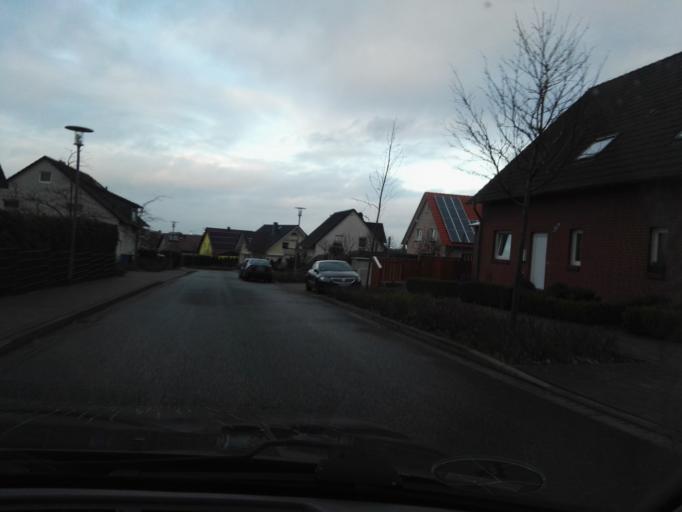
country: DE
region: Lower Saxony
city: Leiferde
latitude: 52.2304
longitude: 10.4758
